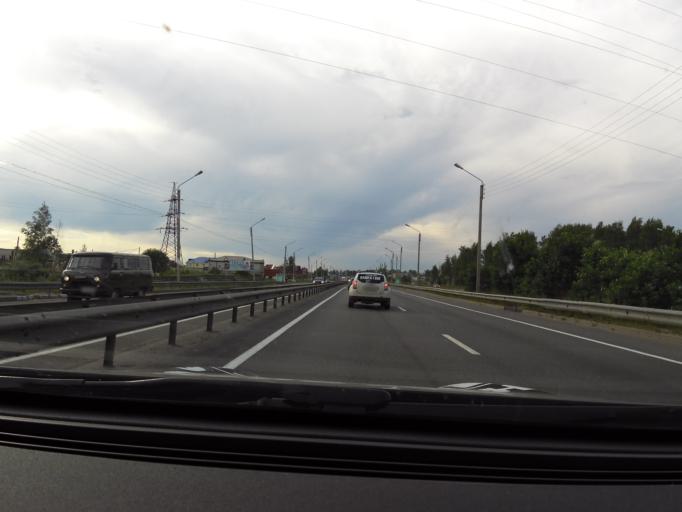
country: RU
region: Vladimir
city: Vyazniki
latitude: 56.2336
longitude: 42.1142
